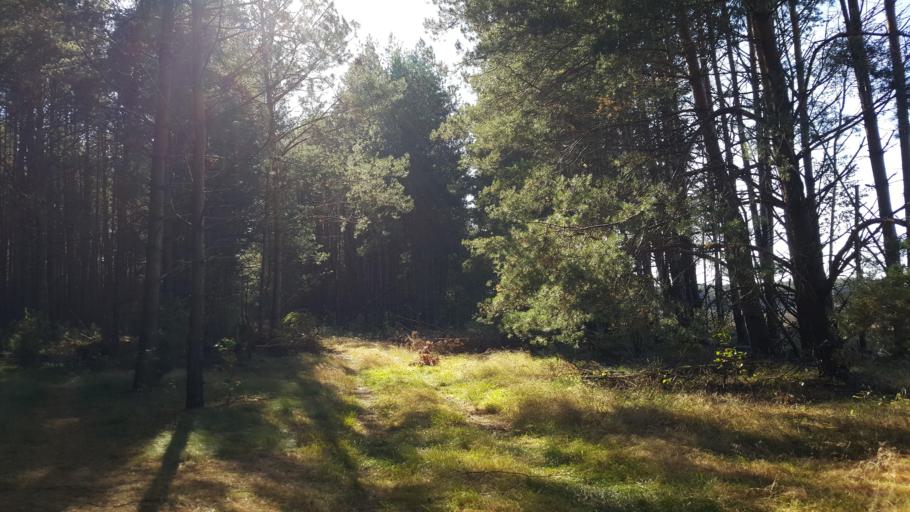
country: BY
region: Brest
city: Kamyanyets
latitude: 52.4322
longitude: 23.9099
